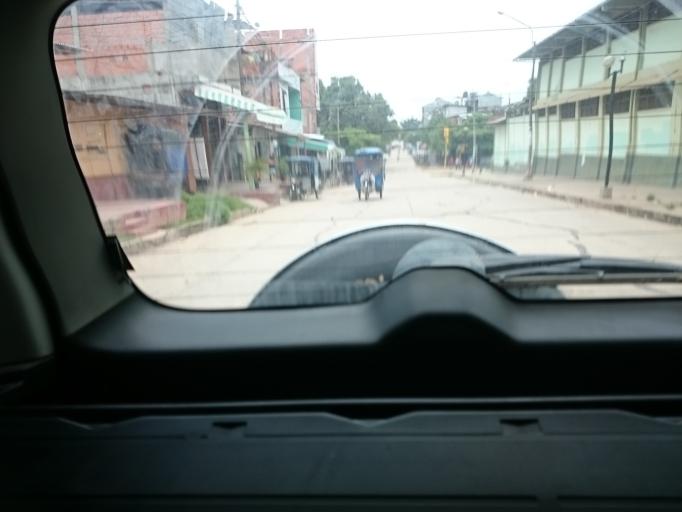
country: PE
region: Ucayali
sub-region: Provincia de Coronel Portillo
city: Pucallpa
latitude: -8.3783
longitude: -74.5321
